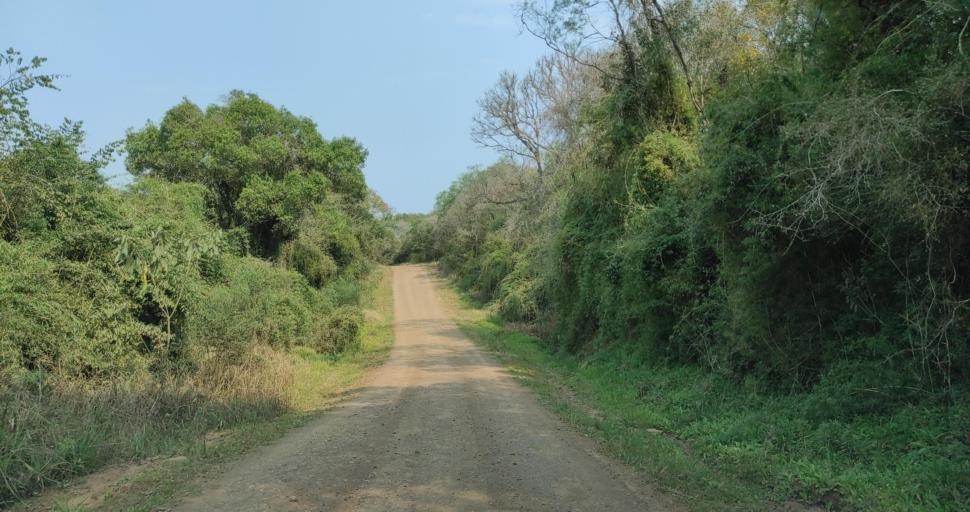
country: AR
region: Misiones
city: Cerro Cora
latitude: -27.5428
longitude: -55.5846
